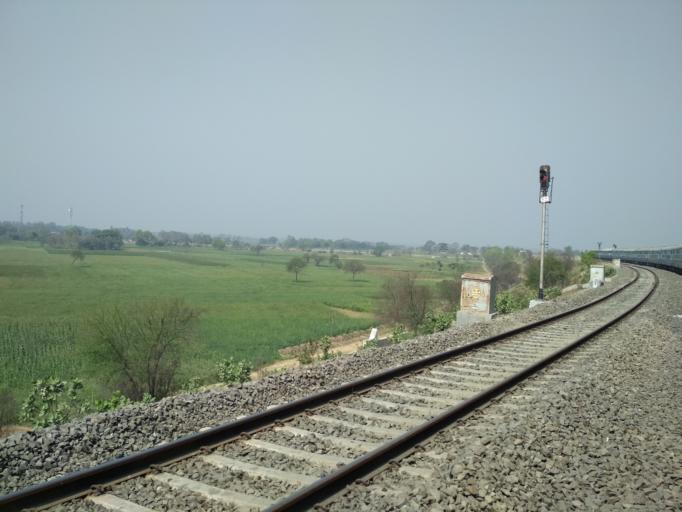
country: IN
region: Bihar
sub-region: Munger
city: Munger
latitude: 25.4338
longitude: 86.4381
